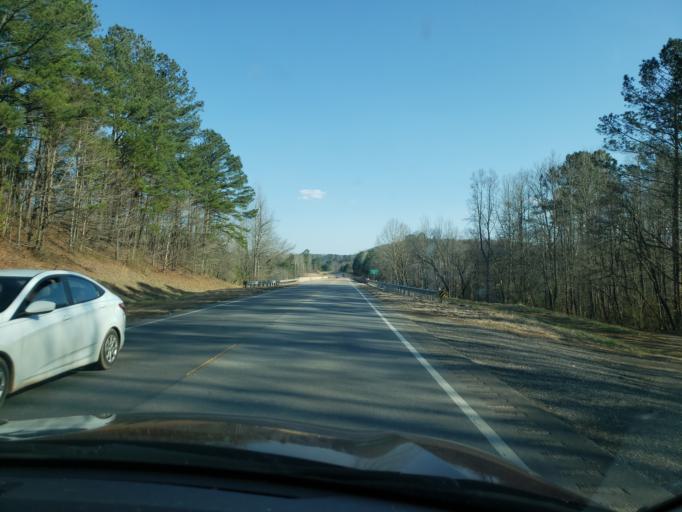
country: US
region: Alabama
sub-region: Cleburne County
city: Heflin
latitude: 33.5105
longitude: -85.6261
